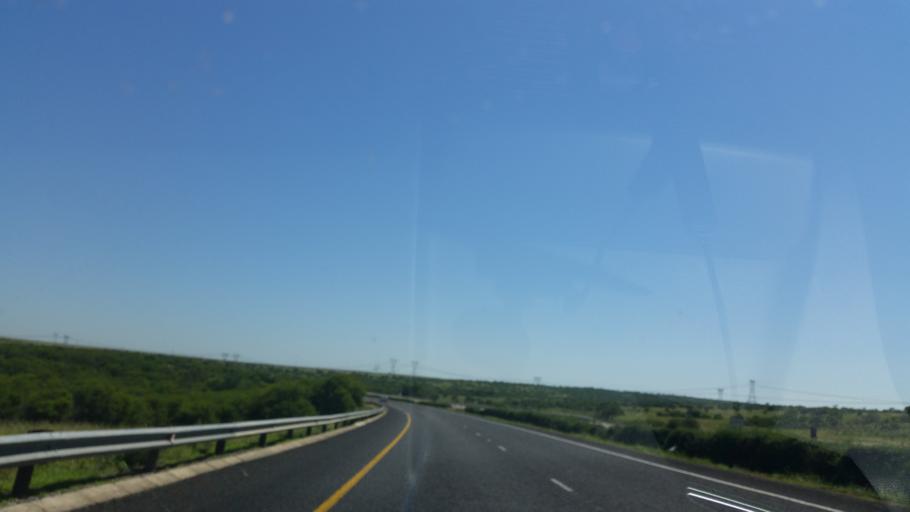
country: ZA
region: KwaZulu-Natal
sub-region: uThukela District Municipality
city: Ladysmith
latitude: -28.6777
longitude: 29.6339
